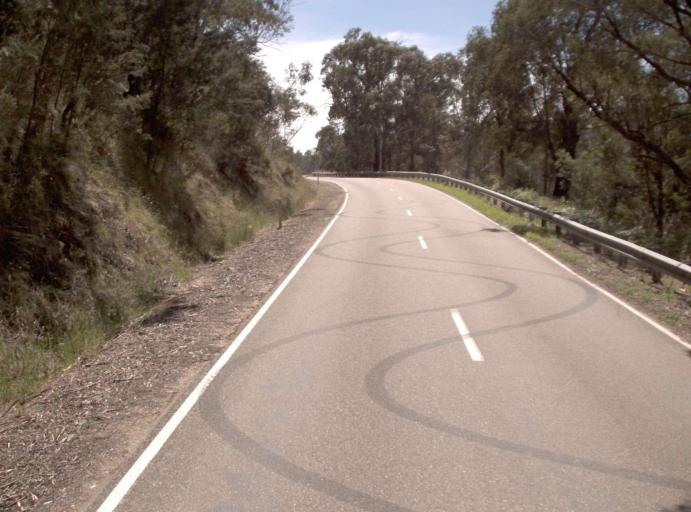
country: AU
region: Victoria
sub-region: Alpine
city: Mount Beauty
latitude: -37.0405
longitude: 147.6357
